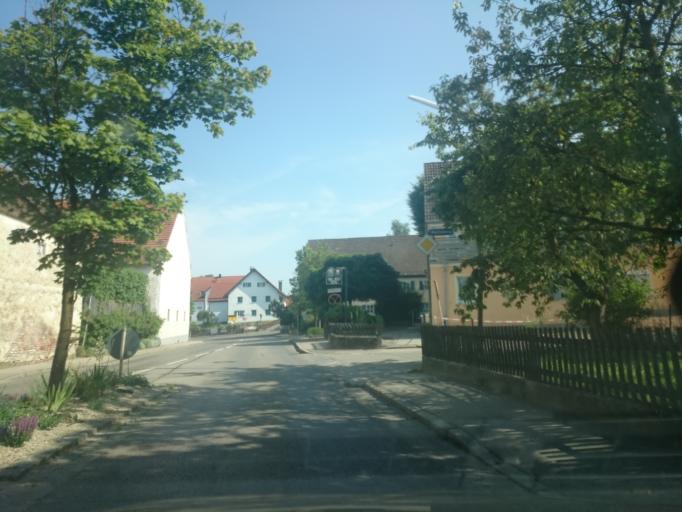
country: DE
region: Bavaria
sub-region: Upper Bavaria
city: Althegnenberg
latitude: 48.2338
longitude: 11.0639
